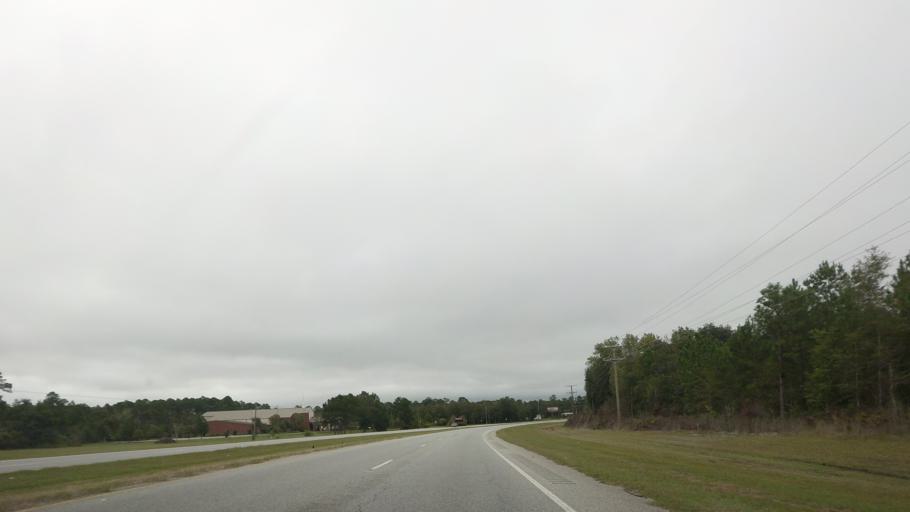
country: US
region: Georgia
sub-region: Lowndes County
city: Valdosta
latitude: 30.8809
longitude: -83.2459
